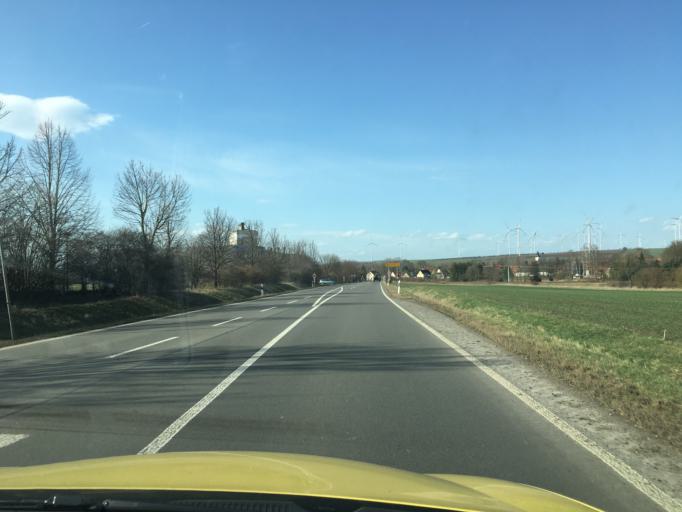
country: DE
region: Thuringia
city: Olbersleben
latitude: 51.1393
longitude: 11.3381
